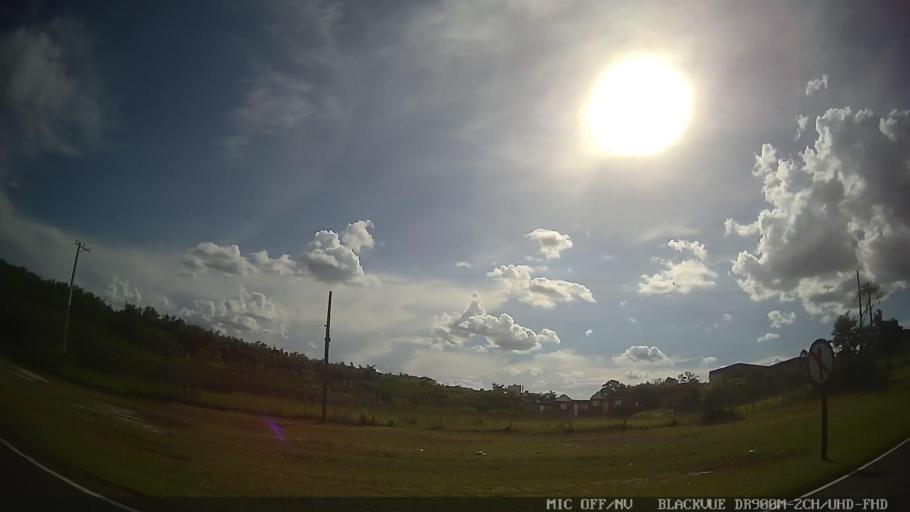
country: BR
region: Sao Paulo
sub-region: Laranjal Paulista
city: Laranjal Paulista
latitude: -23.0460
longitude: -47.8260
